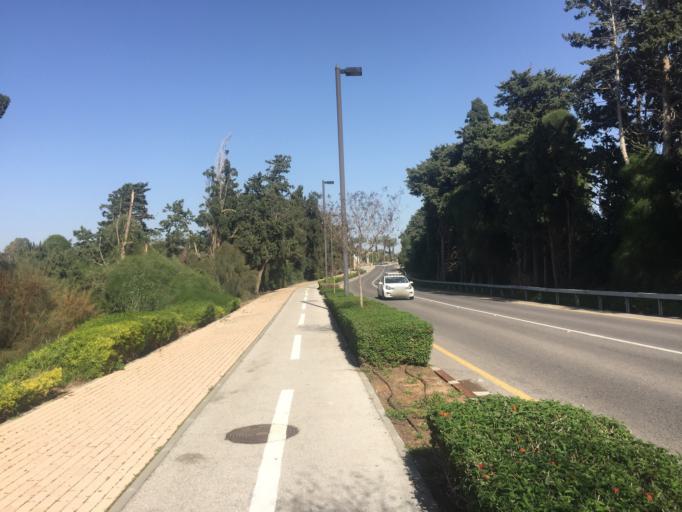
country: IL
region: Haifa
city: Qesarya
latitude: 32.5021
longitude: 34.9022
